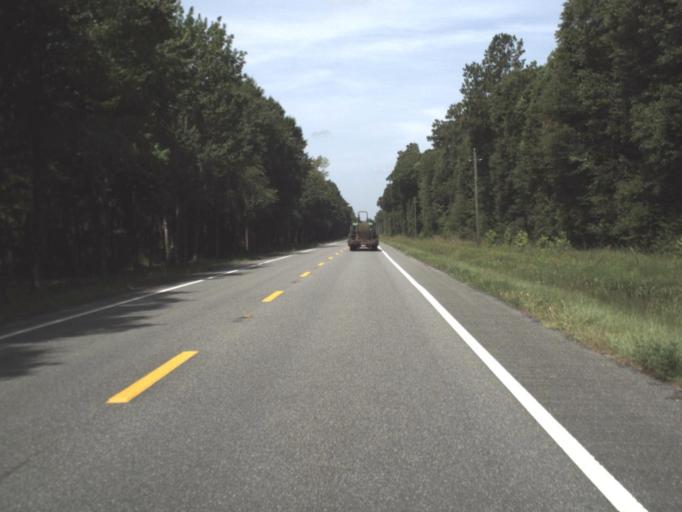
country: US
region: Florida
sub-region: Lafayette County
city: Mayo
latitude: 29.9650
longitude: -83.2276
